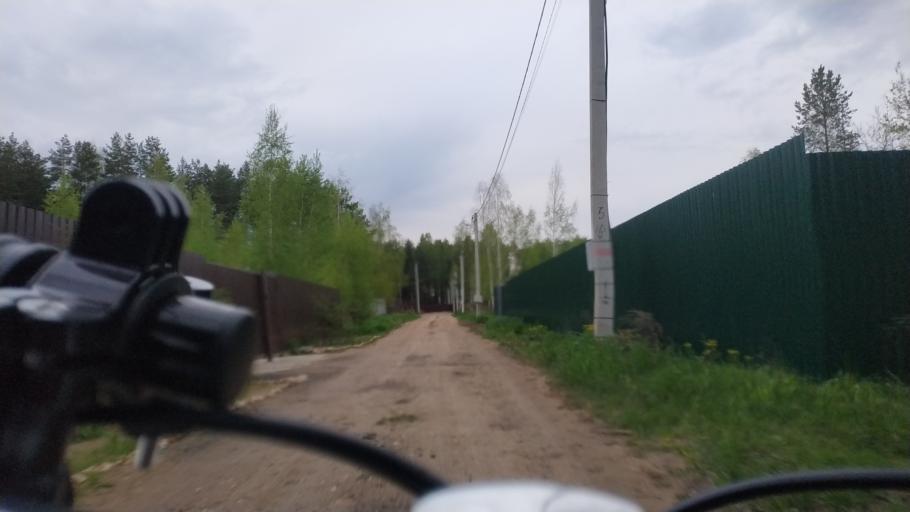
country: RU
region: Moskovskaya
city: Malyshevo
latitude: 55.5608
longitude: 38.3252
